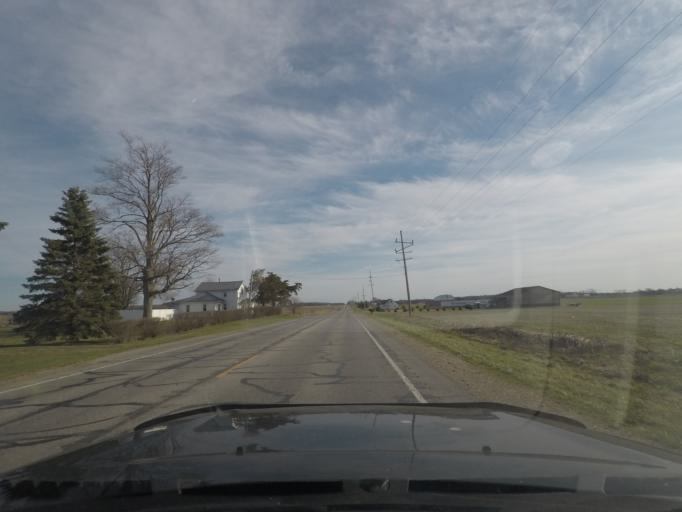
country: US
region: Indiana
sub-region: Elkhart County
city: Wakarusa
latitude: 41.5017
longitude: -86.0020
